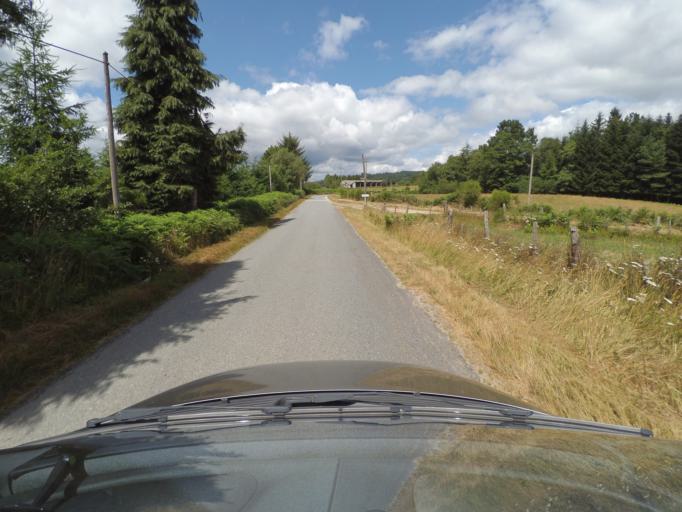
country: FR
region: Limousin
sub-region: Departement de la Creuse
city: Banize
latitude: 45.7832
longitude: 1.9376
